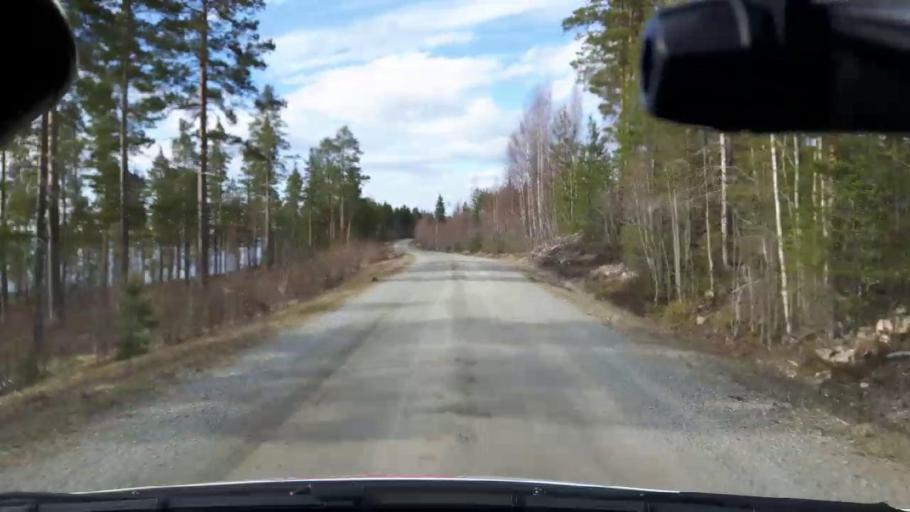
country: SE
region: Jaemtland
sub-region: Bergs Kommun
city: Hoverberg
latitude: 62.7331
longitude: 14.6648
